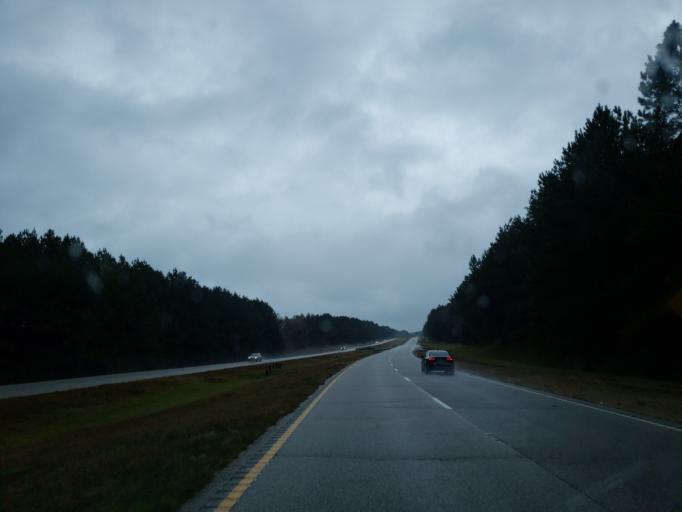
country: US
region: Mississippi
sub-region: Lauderdale County
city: Meridian
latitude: 32.2873
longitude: -88.6982
